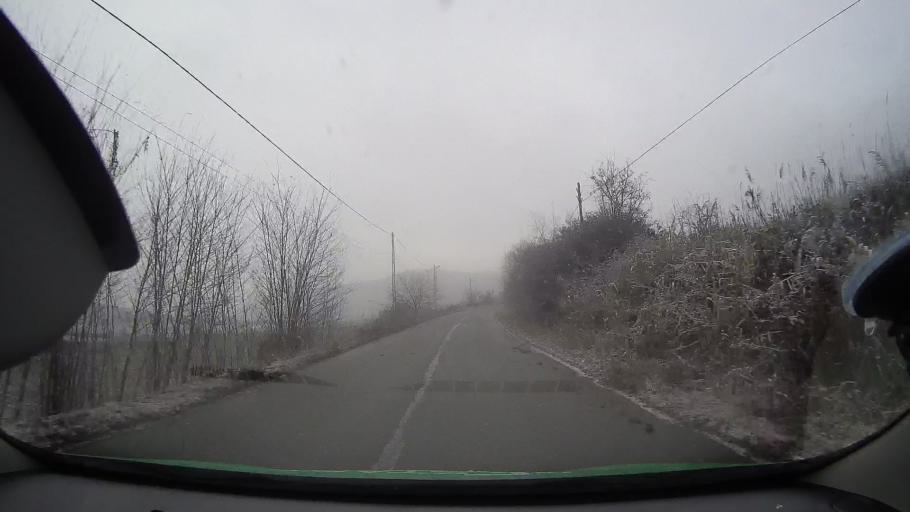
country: RO
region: Alba
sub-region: Comuna Noslac
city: Noslac
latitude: 46.3587
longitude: 23.9310
